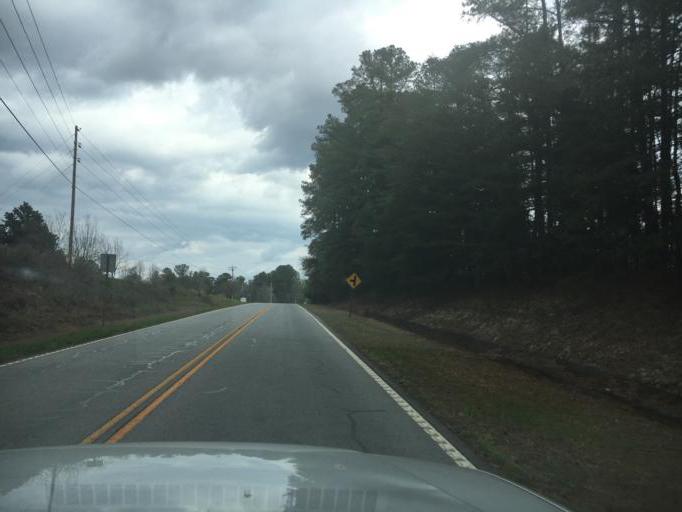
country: US
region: South Carolina
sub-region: Oconee County
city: Westminster
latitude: 34.7107
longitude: -83.0710
